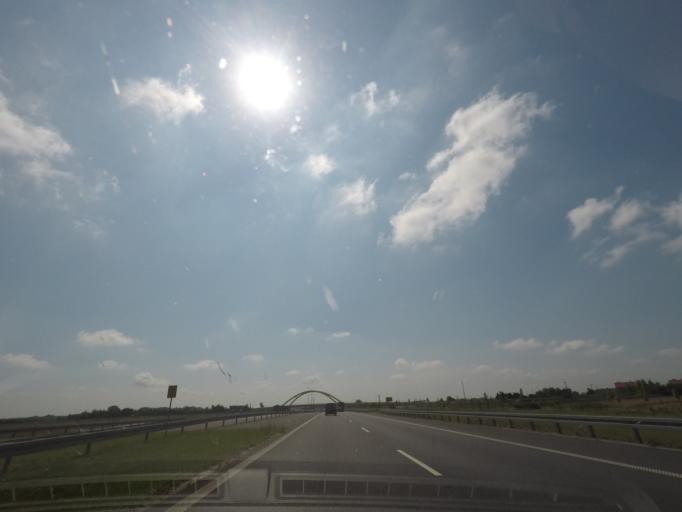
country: PL
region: Kujawsko-Pomorskie
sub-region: Powiat wloclawski
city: Chocen
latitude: 52.5734
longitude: 19.0055
